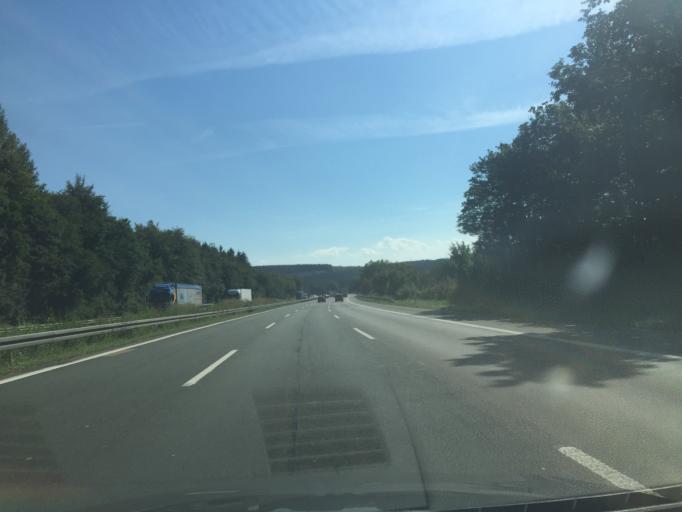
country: DE
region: North Rhine-Westphalia
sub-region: Regierungsbezirk Arnsberg
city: Wilnsdorf
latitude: 50.8044
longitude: 8.0988
